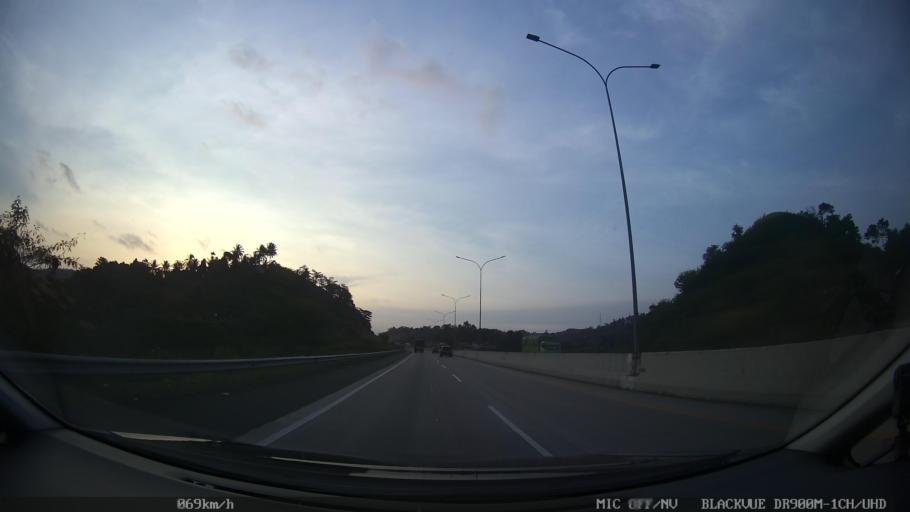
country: ID
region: Lampung
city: Penengahan
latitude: -5.8654
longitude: 105.7456
